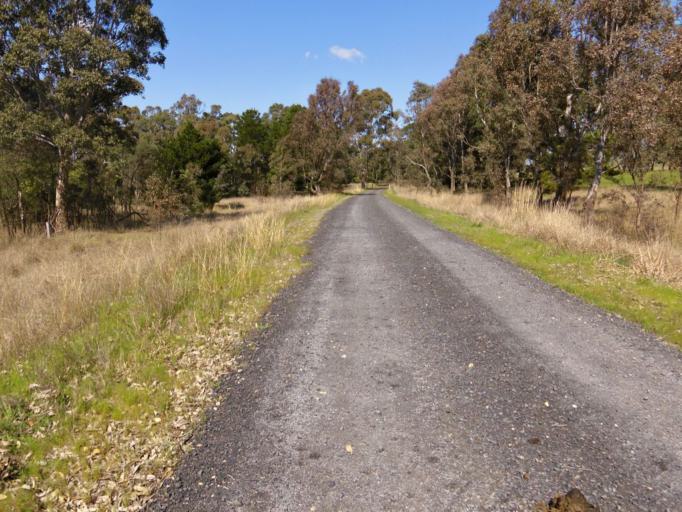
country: AU
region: Victoria
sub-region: Murrindindi
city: Alexandra
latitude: -36.9892
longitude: 145.7357
